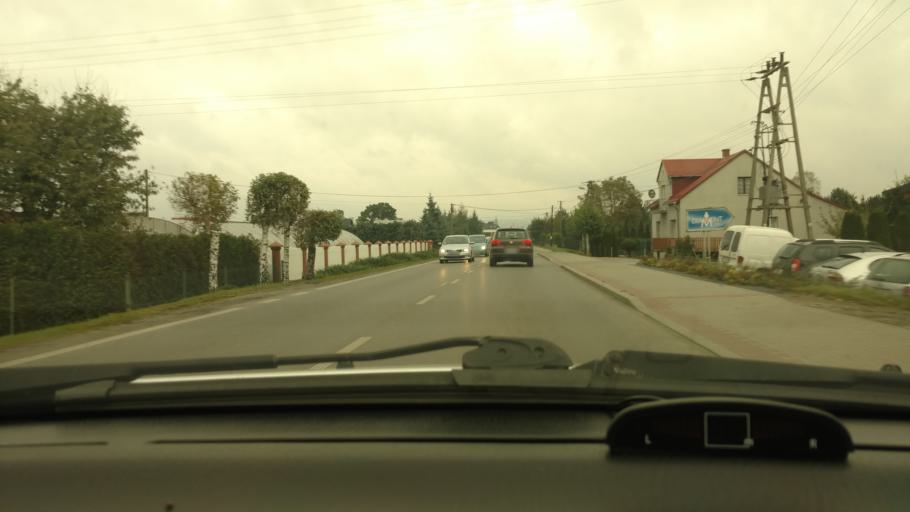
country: PL
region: Lesser Poland Voivodeship
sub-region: Powiat nowosadecki
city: Chelmiec
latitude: 49.6157
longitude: 20.6642
